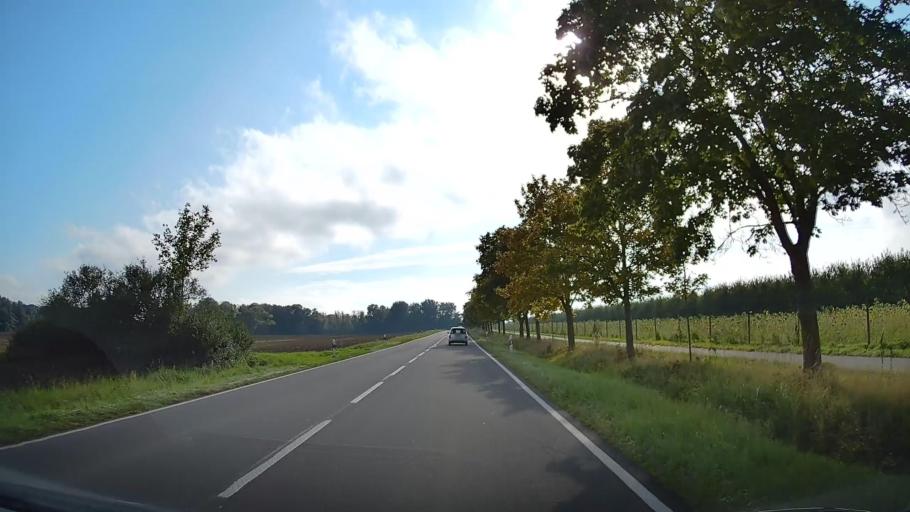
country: DE
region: Mecklenburg-Vorpommern
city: Lubtheen
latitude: 53.3871
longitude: 11.0874
